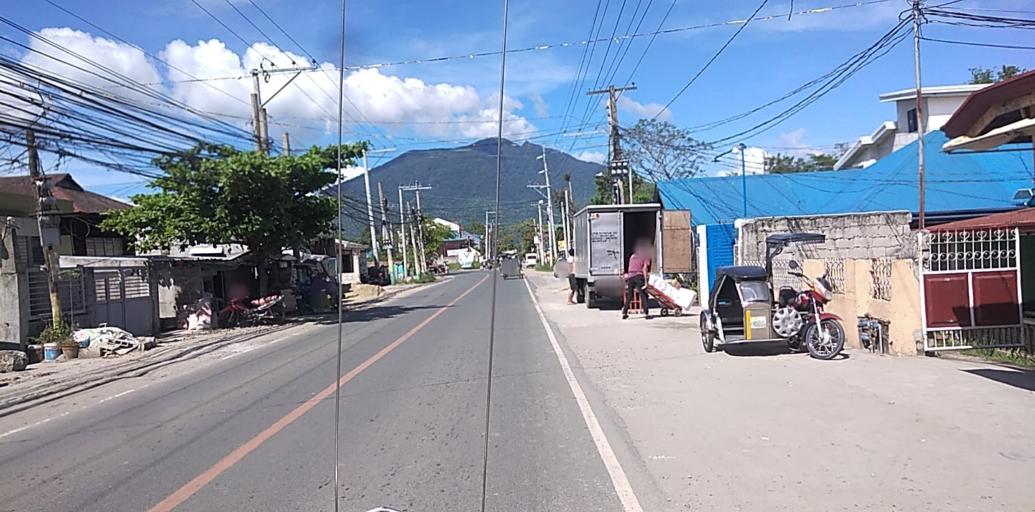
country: PH
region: Central Luzon
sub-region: Province of Pampanga
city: Arayat
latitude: 15.1427
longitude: 120.7716
